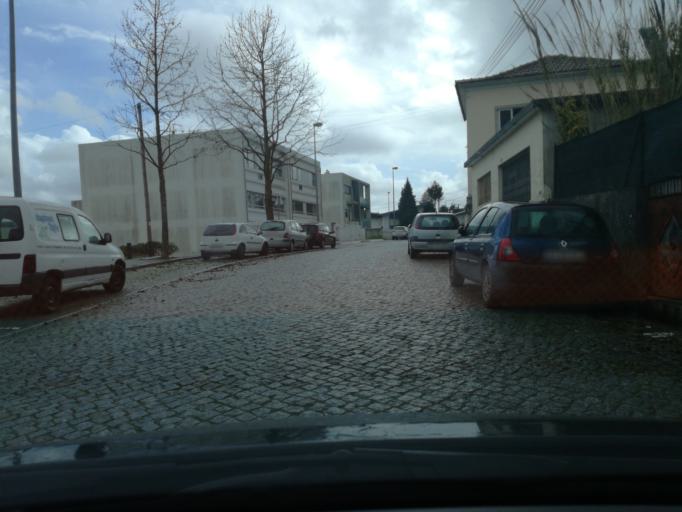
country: PT
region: Porto
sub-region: Valongo
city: Ermesinde
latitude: 41.2415
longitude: -8.5480
